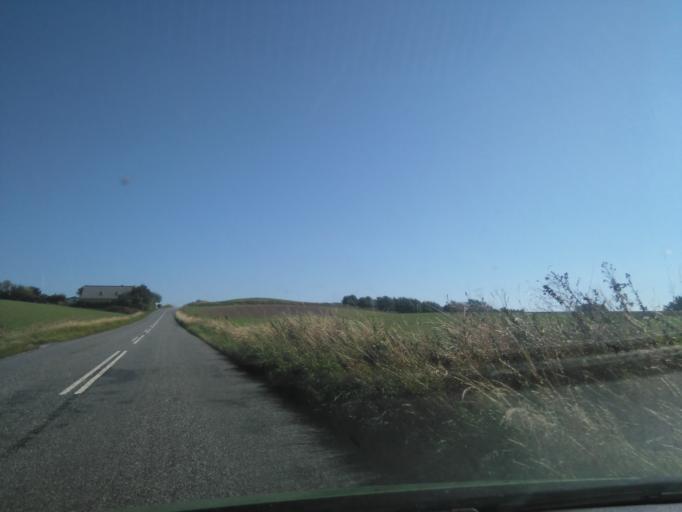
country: DK
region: Central Jutland
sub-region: Syddjurs Kommune
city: Ronde
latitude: 56.1961
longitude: 10.4738
